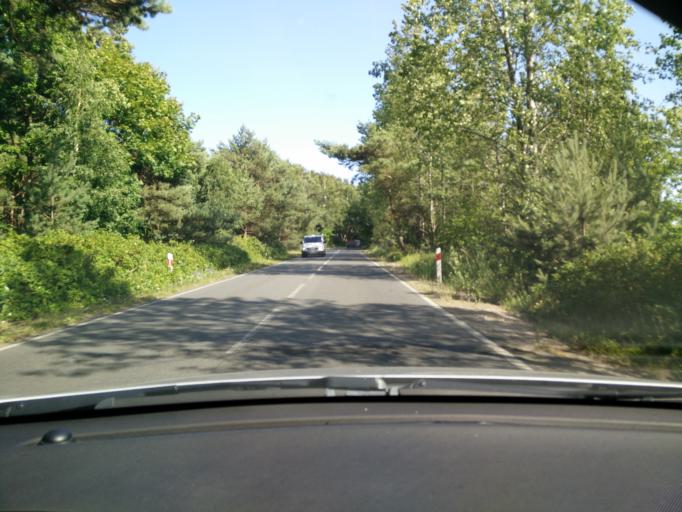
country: PL
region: Pomeranian Voivodeship
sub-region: Powiat pucki
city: Jastarnia
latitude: 54.7184
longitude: 18.6279
